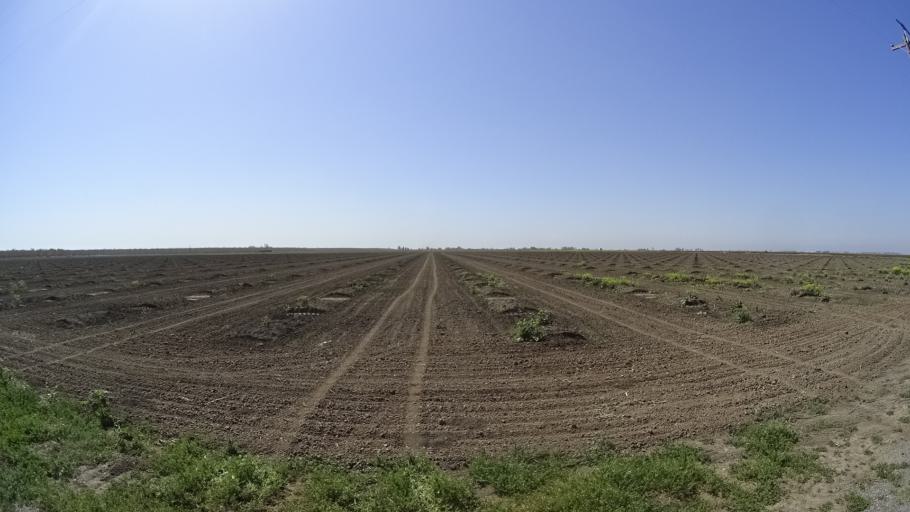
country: US
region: California
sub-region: Glenn County
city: Willows
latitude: 39.4811
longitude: -122.0333
